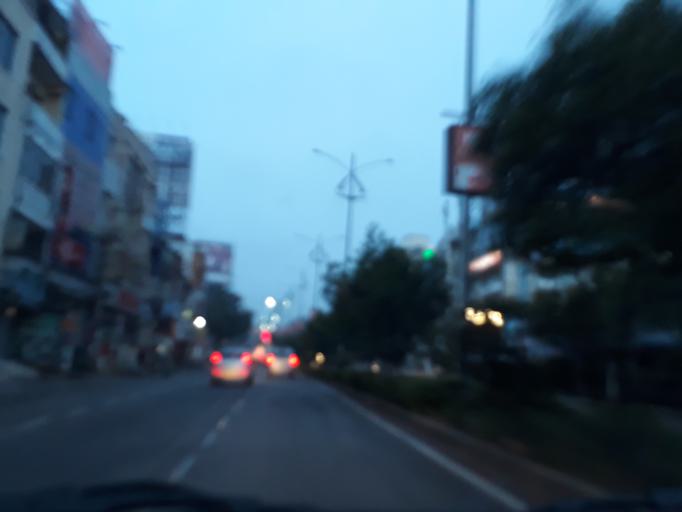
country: IN
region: Telangana
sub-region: Hyderabad
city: Hyderabad
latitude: 17.4258
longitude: 78.4365
